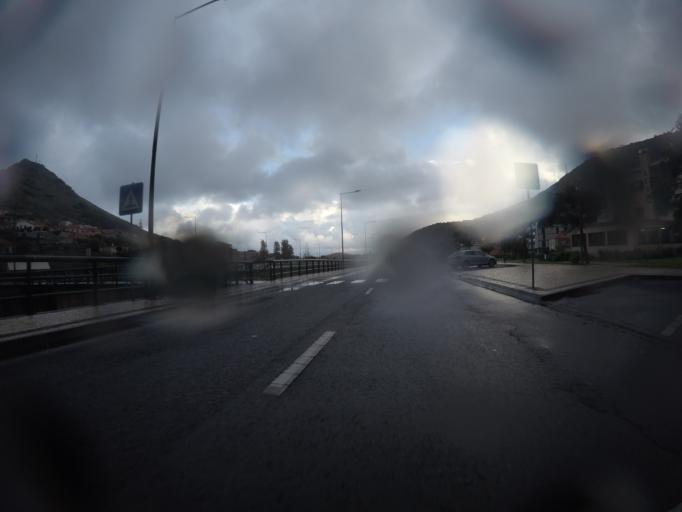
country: PT
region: Madeira
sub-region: Machico
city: Machico
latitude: 32.7232
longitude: -16.7698
